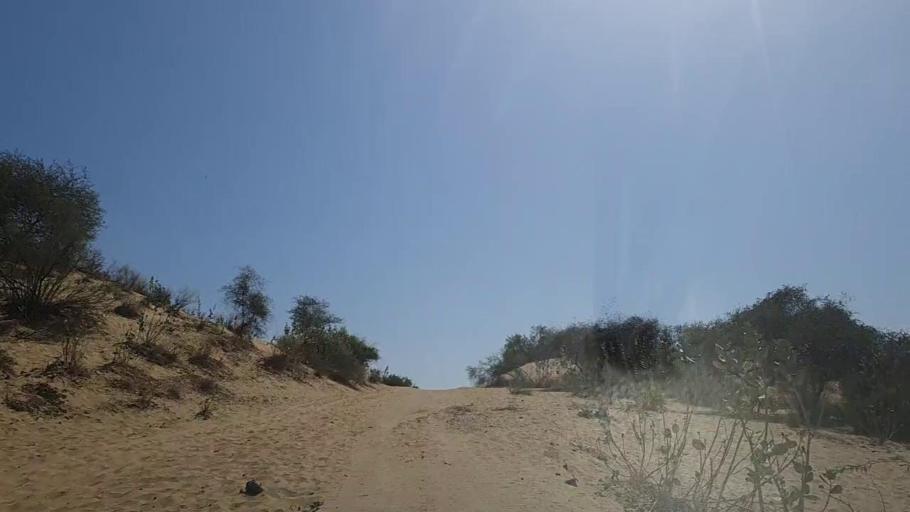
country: PK
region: Sindh
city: Naukot
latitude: 24.8305
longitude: 69.6058
